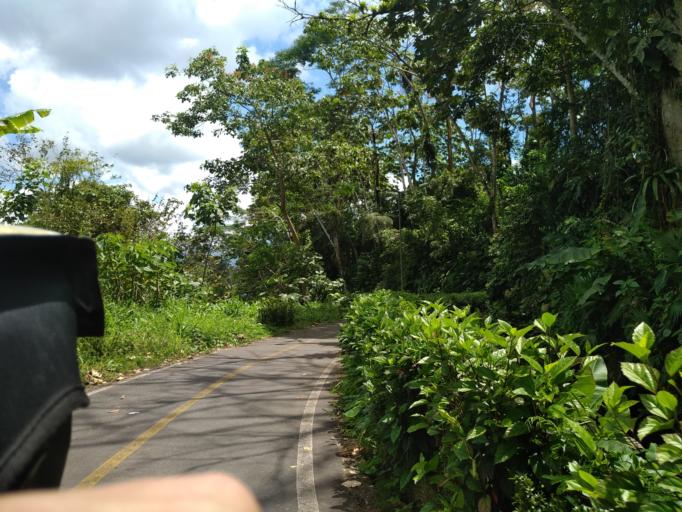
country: EC
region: Napo
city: Tena
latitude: -0.9892
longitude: -77.8208
